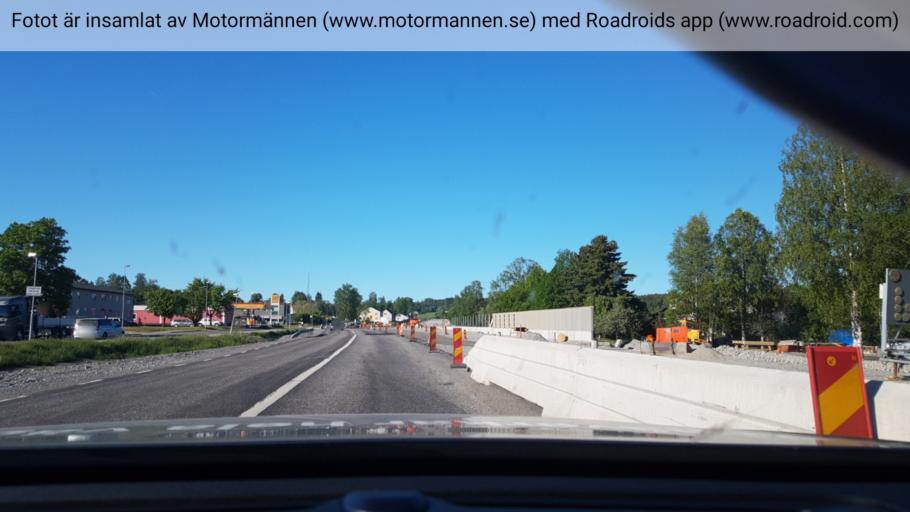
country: SE
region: Vaesternorrland
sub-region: Haernoesands Kommun
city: Haernoesand
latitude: 62.6737
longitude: 17.8404
